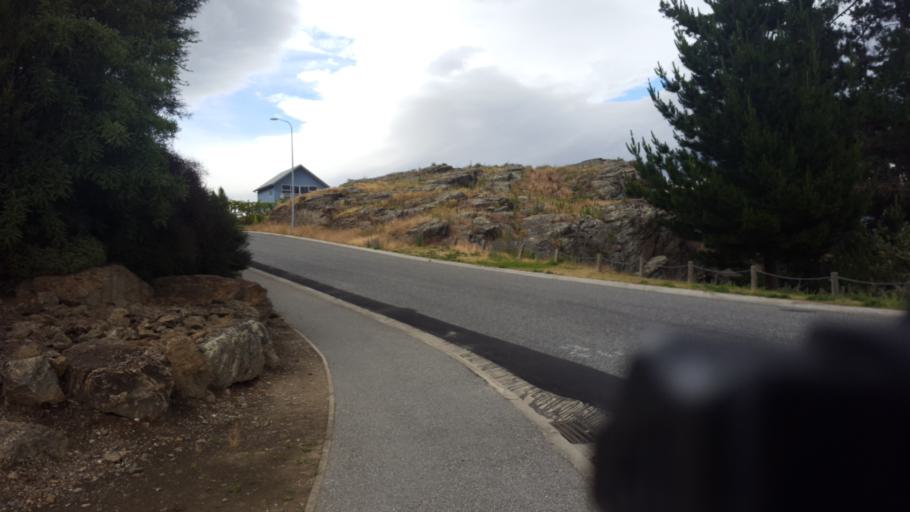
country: NZ
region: Otago
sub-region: Queenstown-Lakes District
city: Wanaka
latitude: -45.2518
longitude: 169.4031
